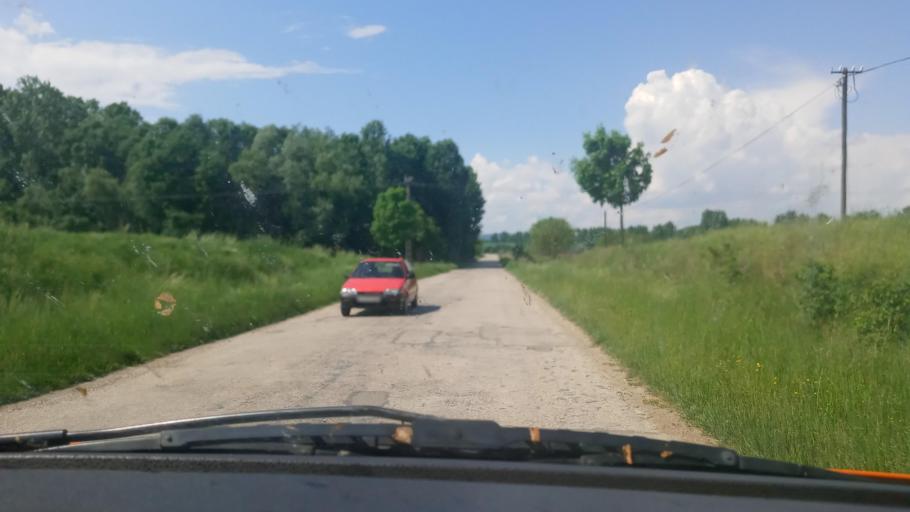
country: HU
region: Baranya
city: Siklos
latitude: 45.8089
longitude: 18.3416
